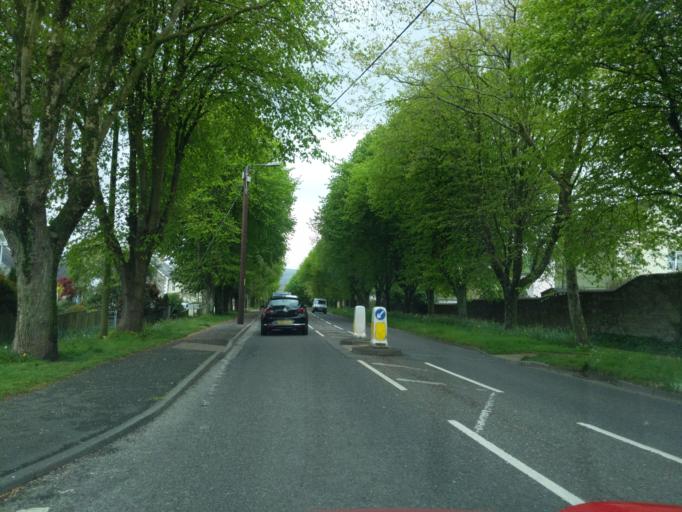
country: GB
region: England
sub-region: Cornwall
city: Bodmin
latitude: 50.4681
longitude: -4.7374
